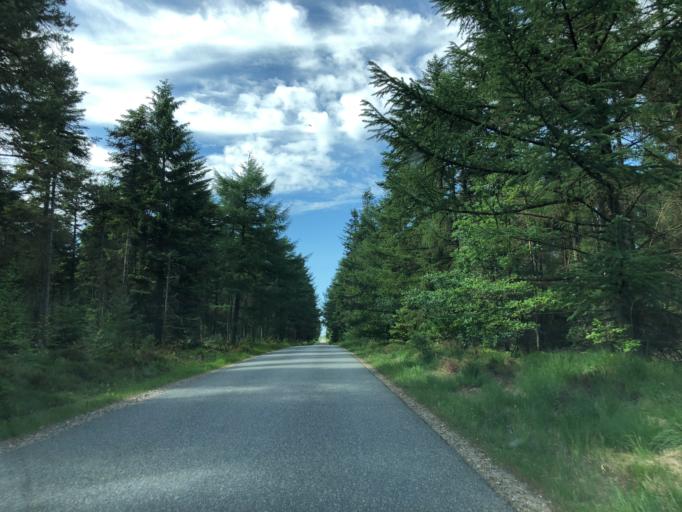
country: DK
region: Central Jutland
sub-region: Herning Kommune
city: Lind
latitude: 56.0415
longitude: 8.9350
